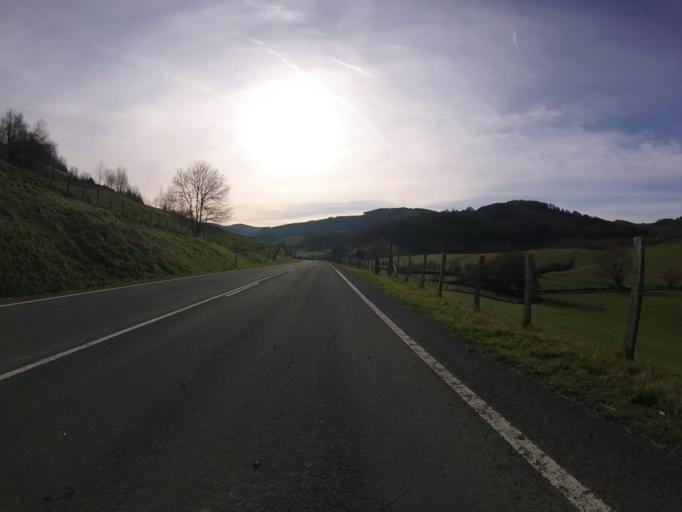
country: ES
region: Basque Country
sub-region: Provincia de Guipuzcoa
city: Berastegui
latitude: 43.1175
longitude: -1.9673
